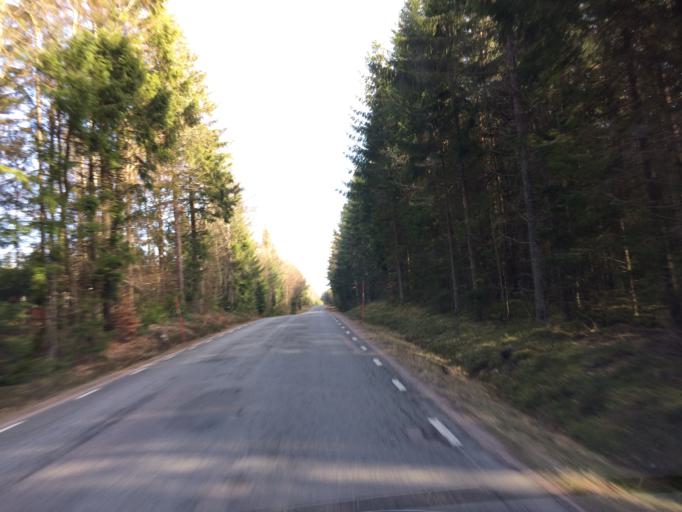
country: SE
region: Kronoberg
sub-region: Ljungby Kommun
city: Ljungby
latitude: 56.6387
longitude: 13.9564
